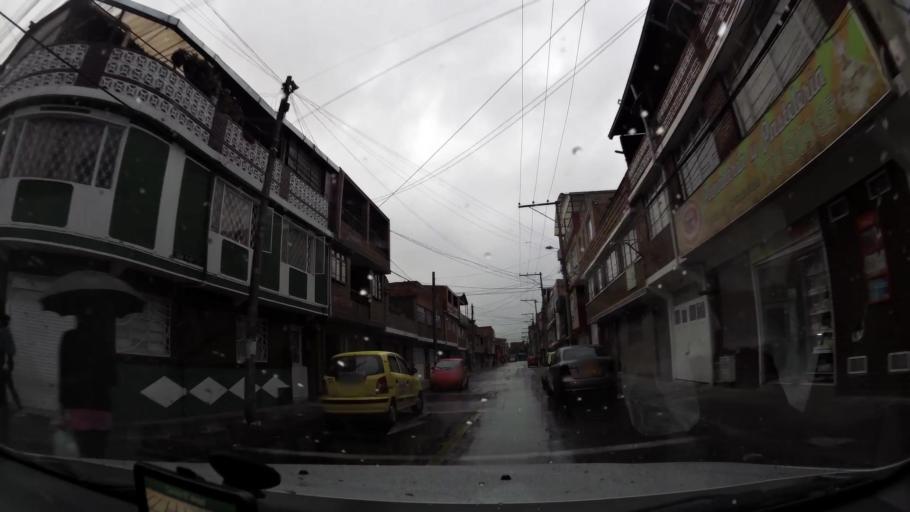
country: CO
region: Bogota D.C.
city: Bogota
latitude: 4.5874
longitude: -74.1387
